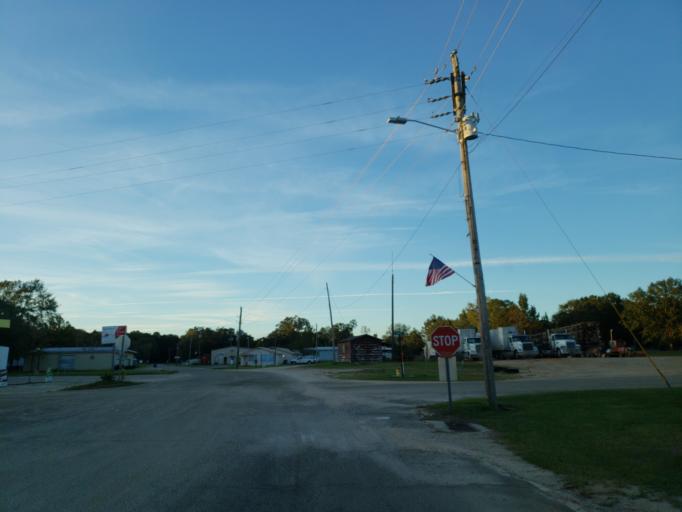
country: US
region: Mississippi
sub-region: Wayne County
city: Belmont
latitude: 31.4361
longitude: -88.4739
